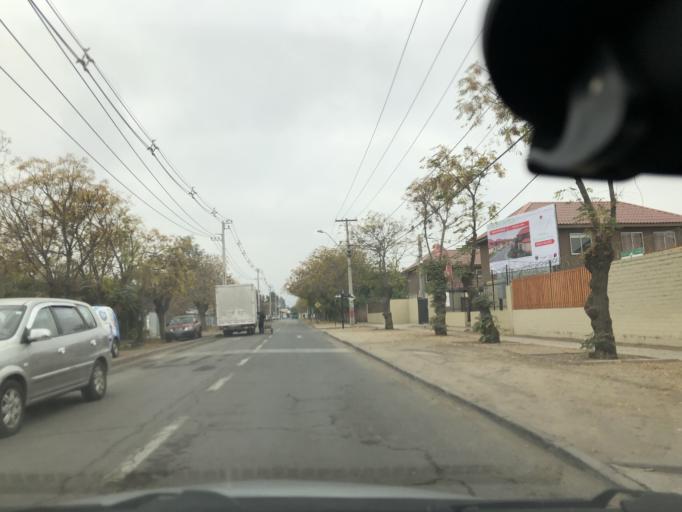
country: CL
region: Santiago Metropolitan
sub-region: Provincia de Santiago
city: La Pintana
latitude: -33.5808
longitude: -70.6094
